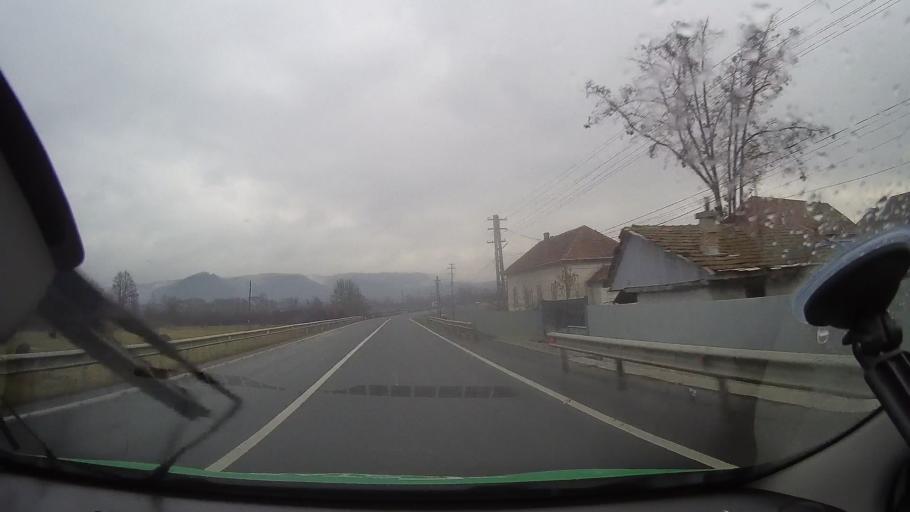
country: RO
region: Hunedoara
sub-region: Comuna Baia de Cris
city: Baia de Cris
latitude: 46.1780
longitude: 22.7010
